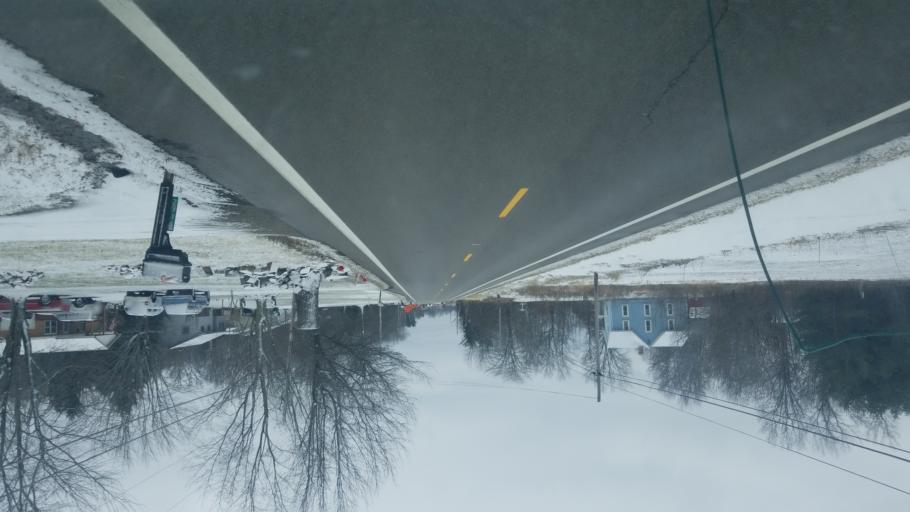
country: US
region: Ohio
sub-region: Licking County
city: Johnstown
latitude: 40.1843
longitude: -82.7492
